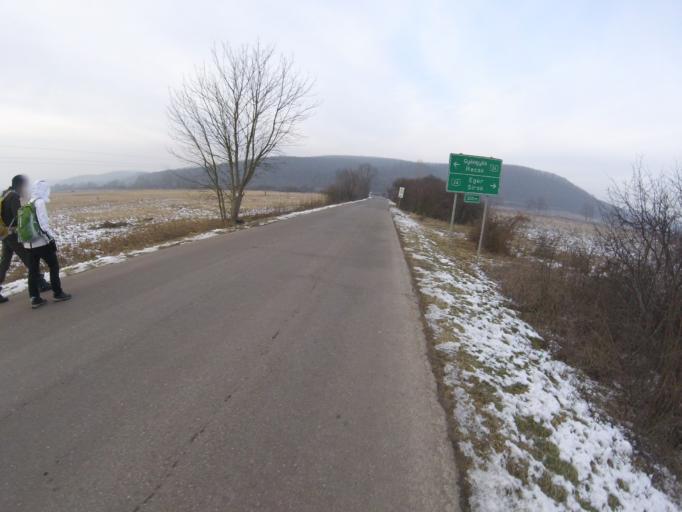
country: HU
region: Heves
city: Sirok
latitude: 47.9179
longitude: 20.1773
